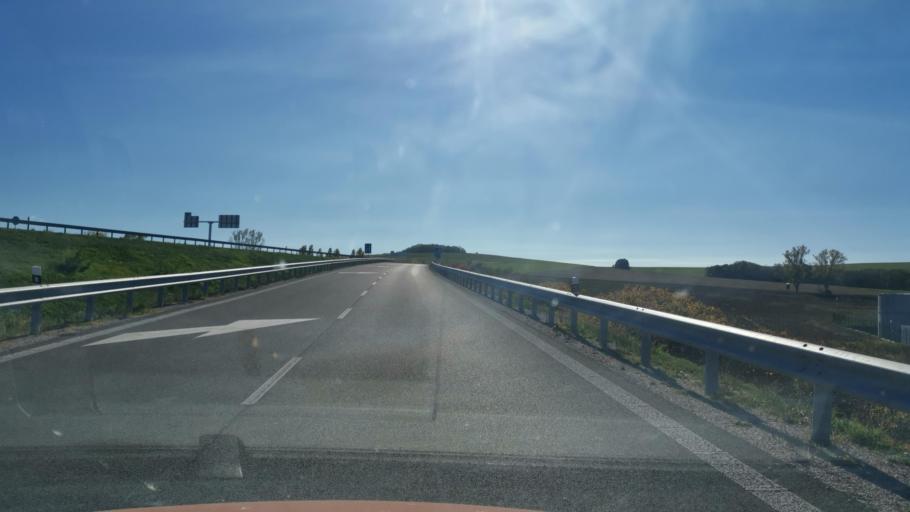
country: HU
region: Borsod-Abauj-Zemplen
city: Gonc
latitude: 48.5471
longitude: 21.2314
